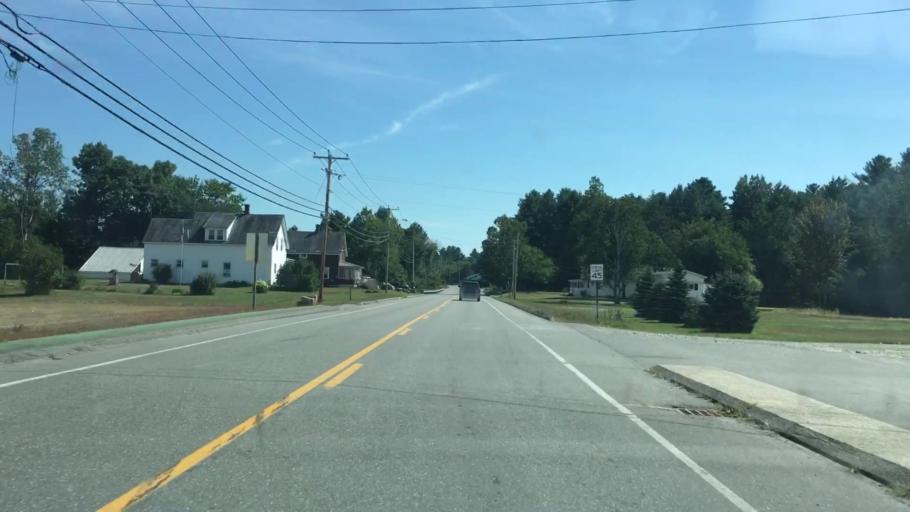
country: US
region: Maine
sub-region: Piscataquis County
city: Milo
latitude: 45.2452
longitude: -68.9759
